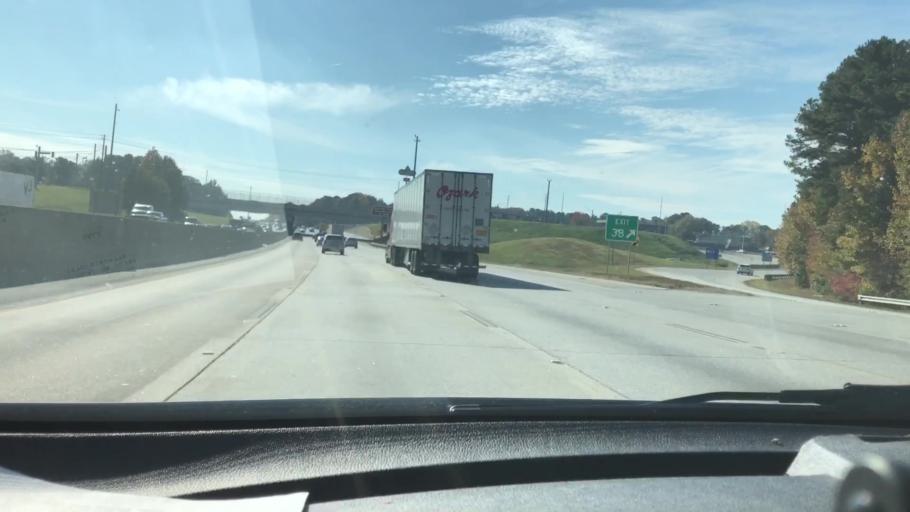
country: US
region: Georgia
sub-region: DeKalb County
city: Clarkston
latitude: 33.8299
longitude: -84.2530
